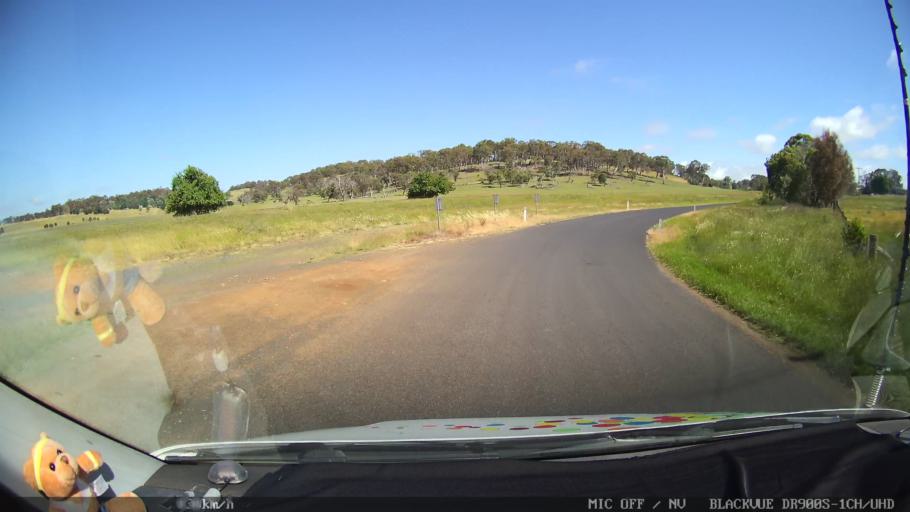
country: AU
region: New South Wales
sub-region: Guyra
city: Guyra
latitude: -30.1230
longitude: 151.6864
